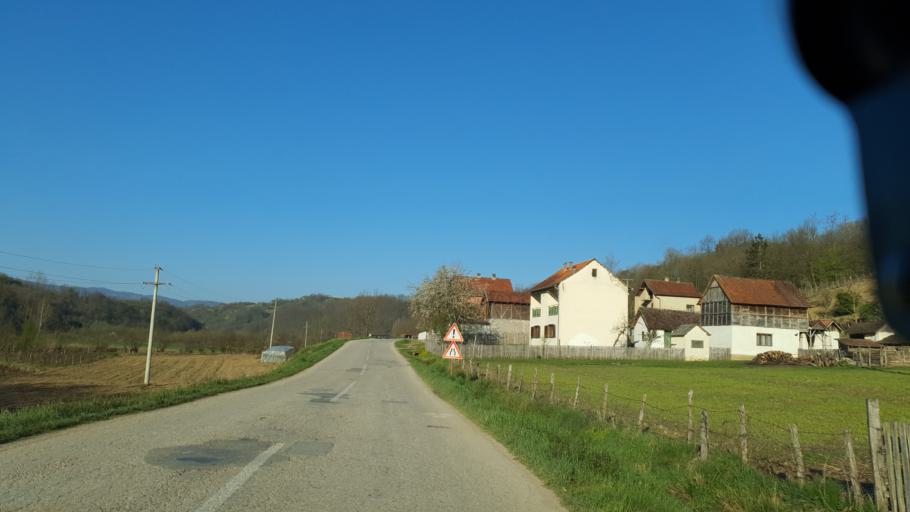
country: RS
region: Central Serbia
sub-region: Kolubarski Okrug
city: Osecina
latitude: 44.3584
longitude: 19.5357
